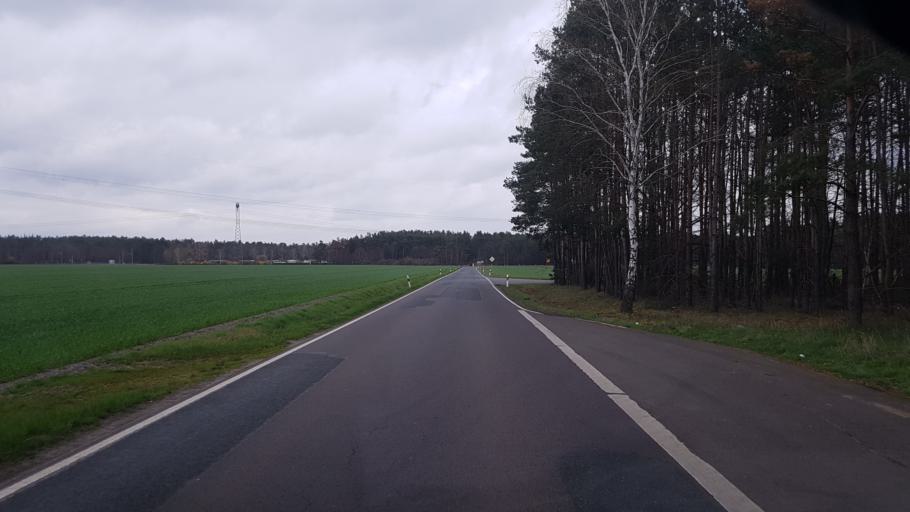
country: DE
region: Brandenburg
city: Hohenbocka
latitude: 51.4531
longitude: 13.9828
